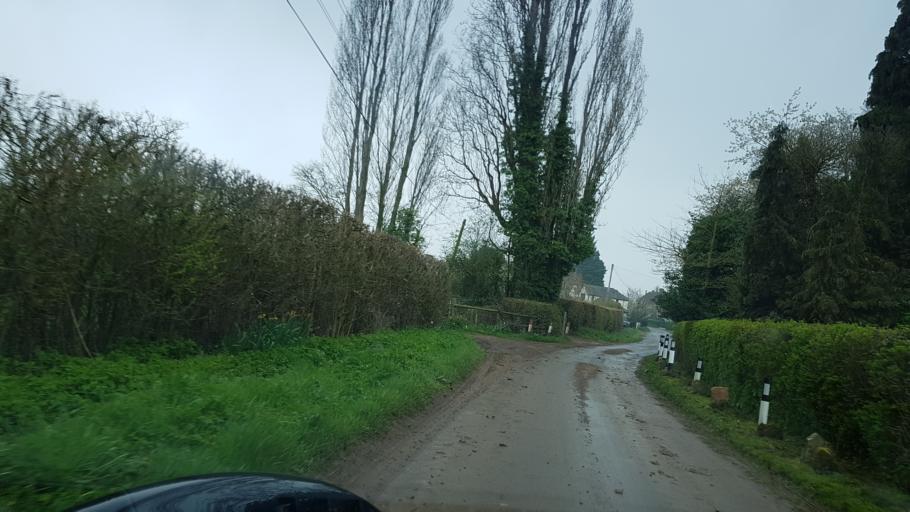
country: GB
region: England
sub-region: Herefordshire
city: Yatton
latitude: 52.0211
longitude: -2.5218
